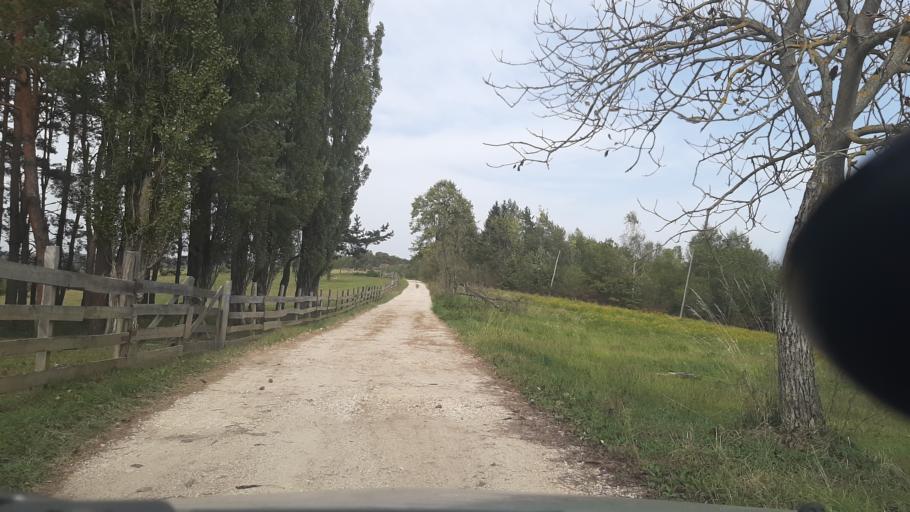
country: BA
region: Republika Srpska
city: Maglajani
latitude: 44.8797
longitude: 17.4739
